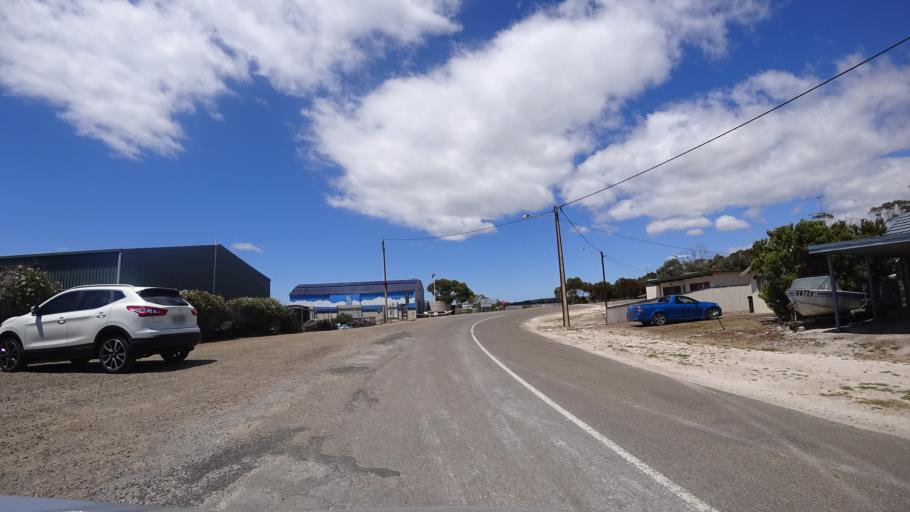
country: AU
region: South Australia
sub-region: Kangaroo Island
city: Kingscote
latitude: -35.7861
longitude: 137.7726
